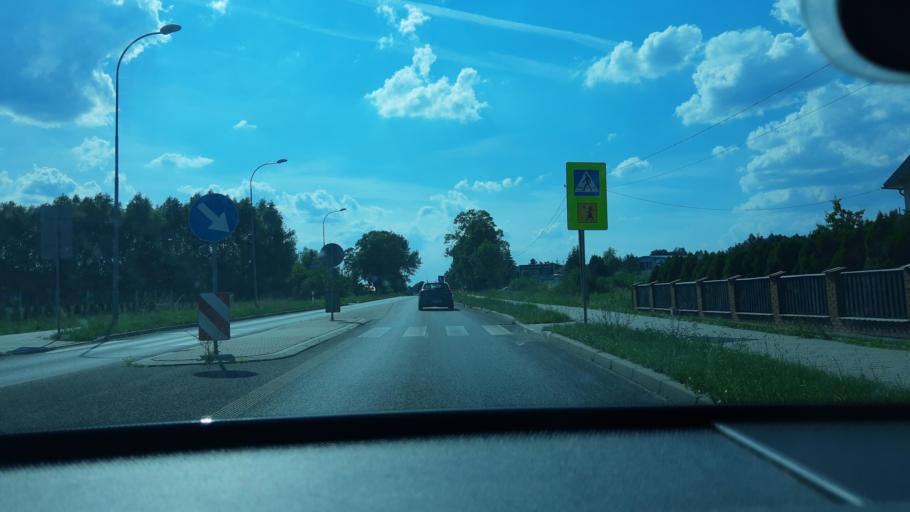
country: PL
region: Lodz Voivodeship
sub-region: Powiat zdunskowolski
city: Zdunska Wola
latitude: 51.6078
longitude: 18.9085
